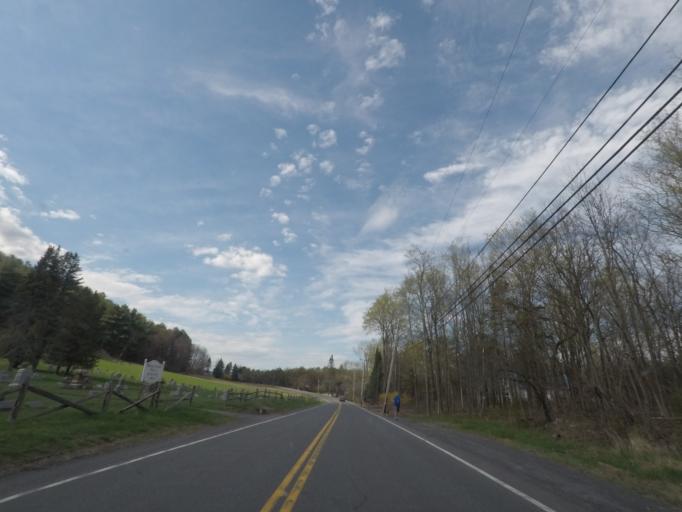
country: US
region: New York
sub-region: Albany County
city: Voorheesville
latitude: 42.5611
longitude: -73.9514
